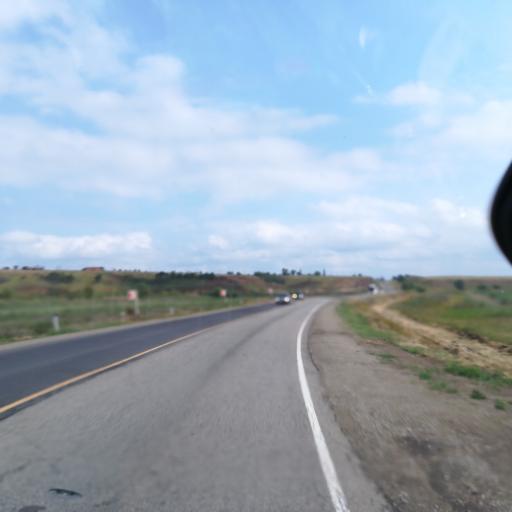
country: RU
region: Krasnodarskiy
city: Varenikovskaya
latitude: 45.1765
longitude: 37.6526
